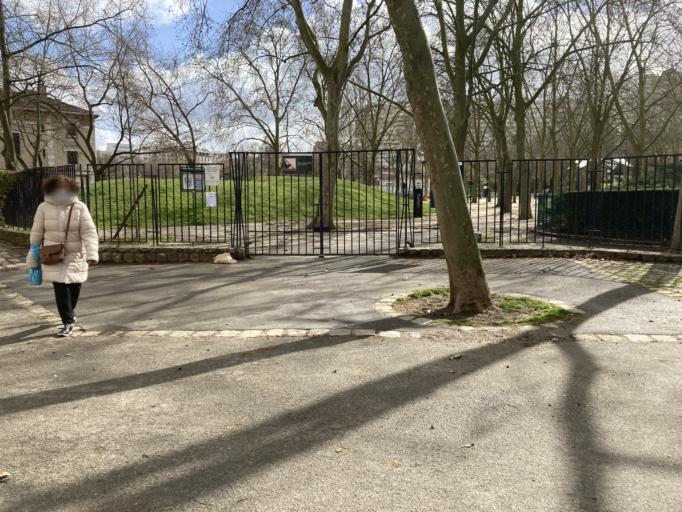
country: FR
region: Ile-de-France
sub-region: Departement des Hauts-de-Seine
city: Malakoff
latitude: 48.8331
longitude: 2.2995
